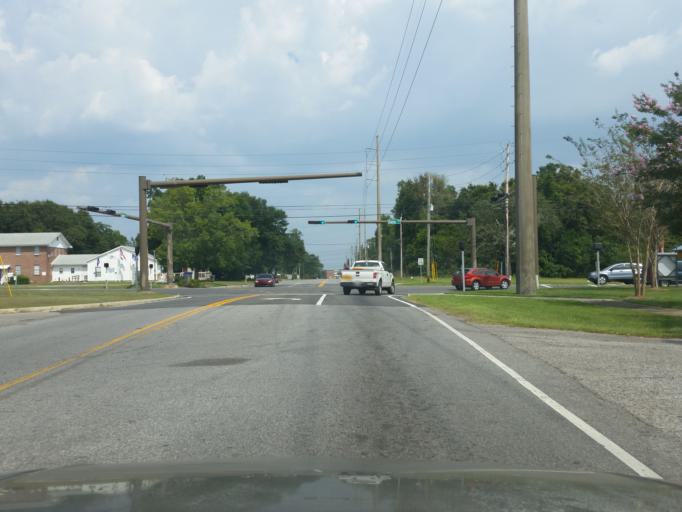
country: US
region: Florida
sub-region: Escambia County
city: Ferry Pass
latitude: 30.5298
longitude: -87.2089
